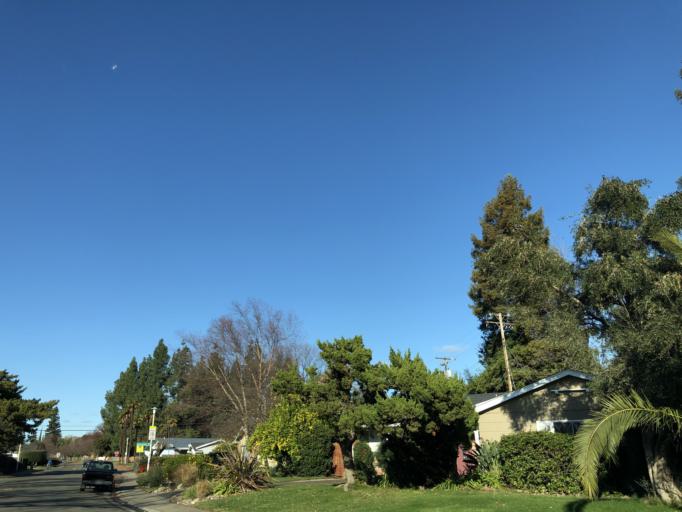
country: US
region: California
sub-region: Sacramento County
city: Rosemont
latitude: 38.5515
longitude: -121.3998
